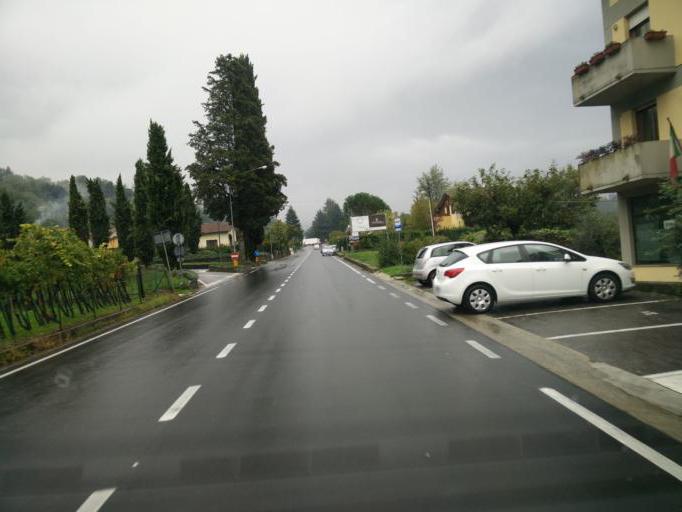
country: IT
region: Tuscany
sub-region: Provincia di Lucca
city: Barga
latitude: 44.0828
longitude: 10.4635
